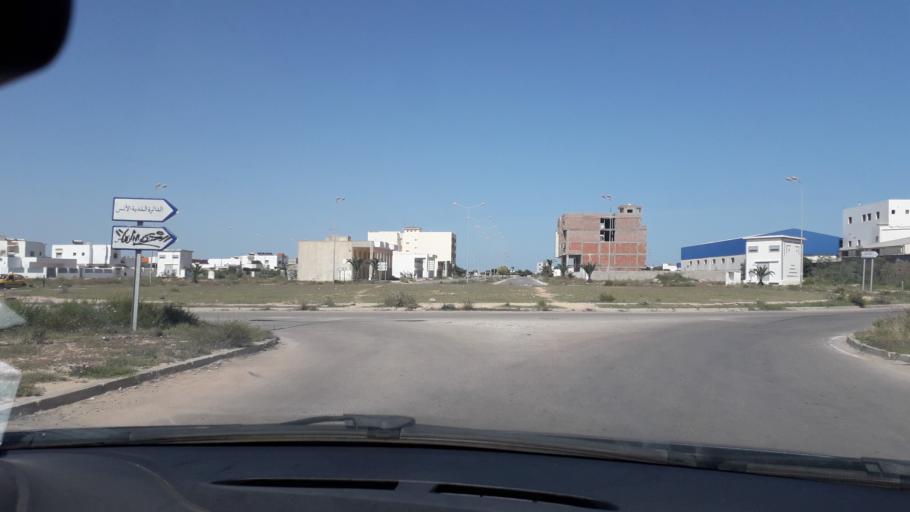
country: TN
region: Safaqis
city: Al Qarmadah
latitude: 34.8346
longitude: 10.7613
